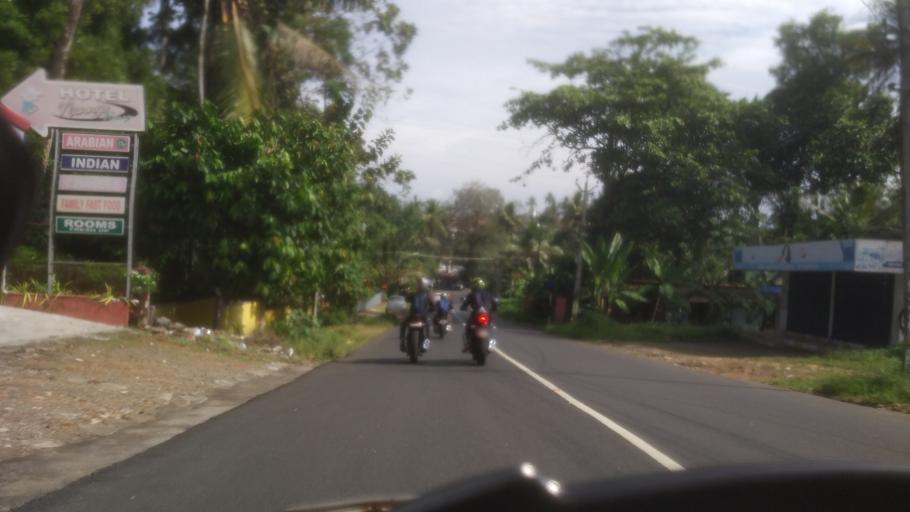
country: IN
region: Kerala
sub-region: Ernakulam
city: Kotamangalam
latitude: 10.0590
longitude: 76.6840
